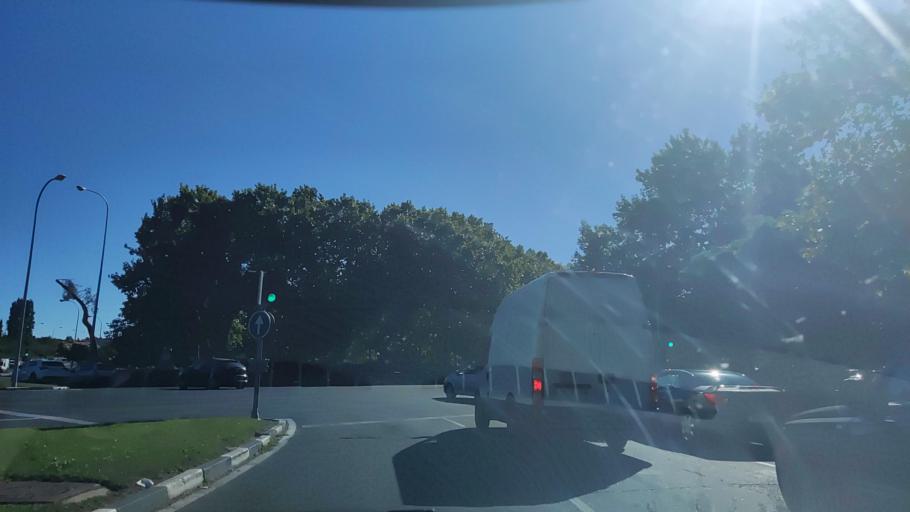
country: ES
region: Madrid
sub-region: Provincia de Madrid
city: Latina
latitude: 40.3739
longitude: -3.7341
